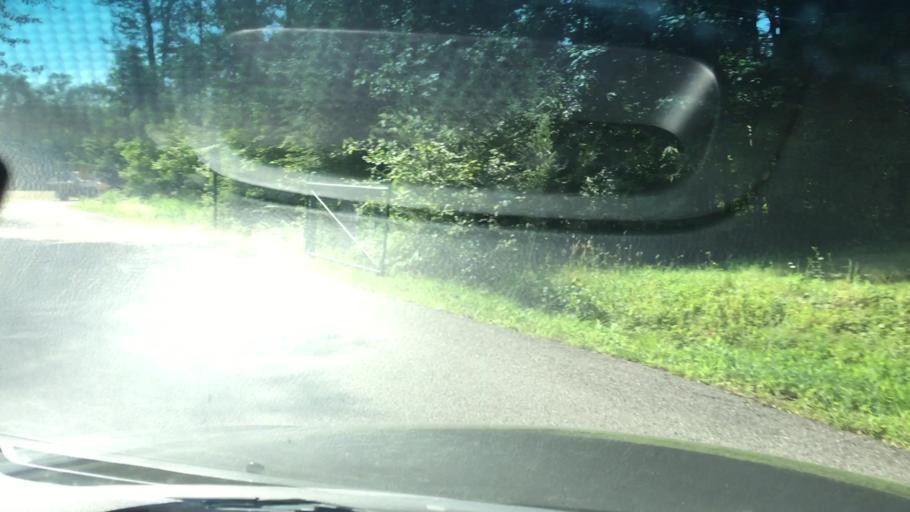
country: US
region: Pennsylvania
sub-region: Luzerne County
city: Harleigh
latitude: 41.0396
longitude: -75.9783
